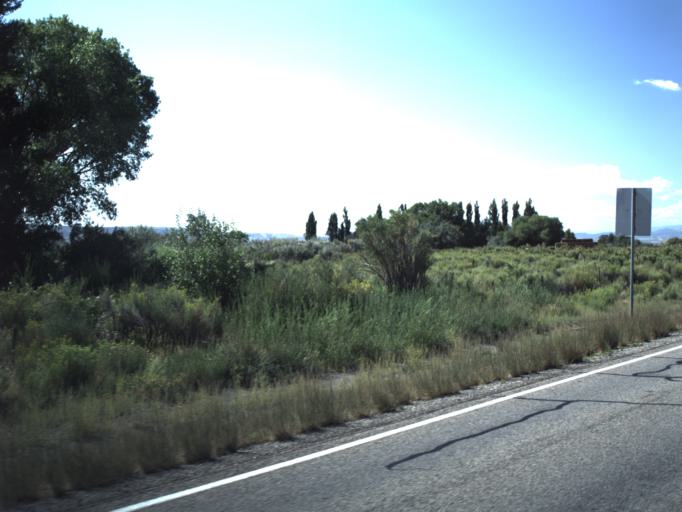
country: US
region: Utah
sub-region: Emery County
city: Ferron
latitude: 38.9179
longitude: -111.2630
